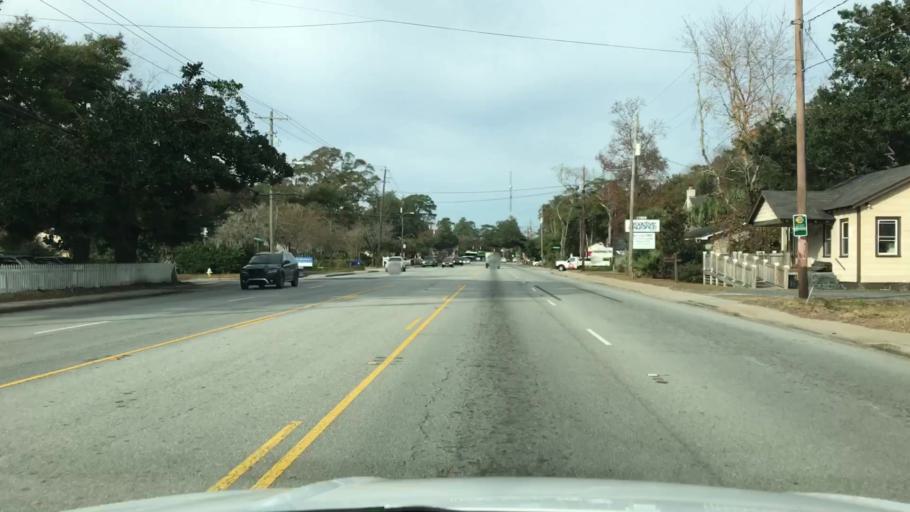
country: US
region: South Carolina
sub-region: Charleston County
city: North Charleston
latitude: 32.7997
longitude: -80.0114
